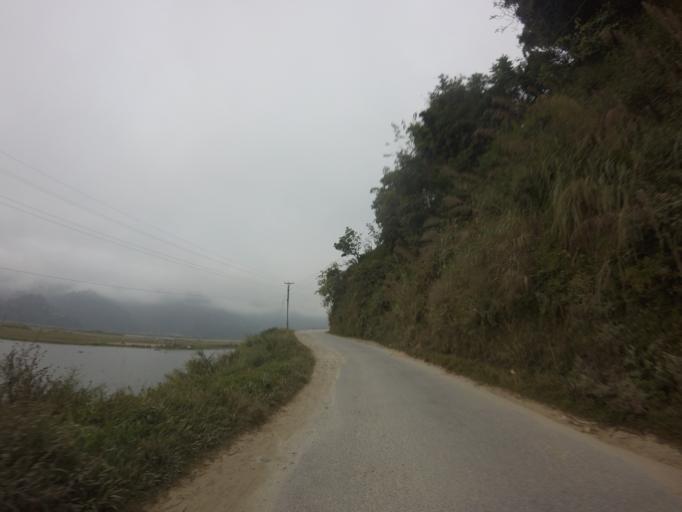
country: NP
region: Western Region
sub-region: Gandaki Zone
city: Pokhara
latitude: 28.2279
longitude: 83.9347
